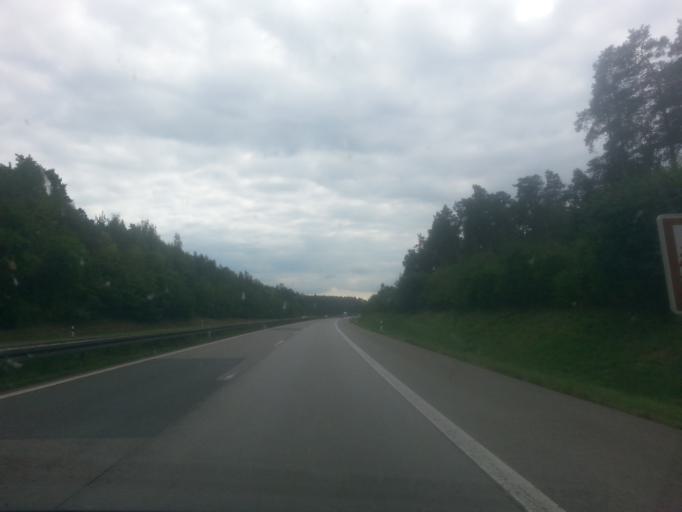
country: DE
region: Bavaria
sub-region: Upper Palatinate
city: Teublitz
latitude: 49.2404
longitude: 12.1326
